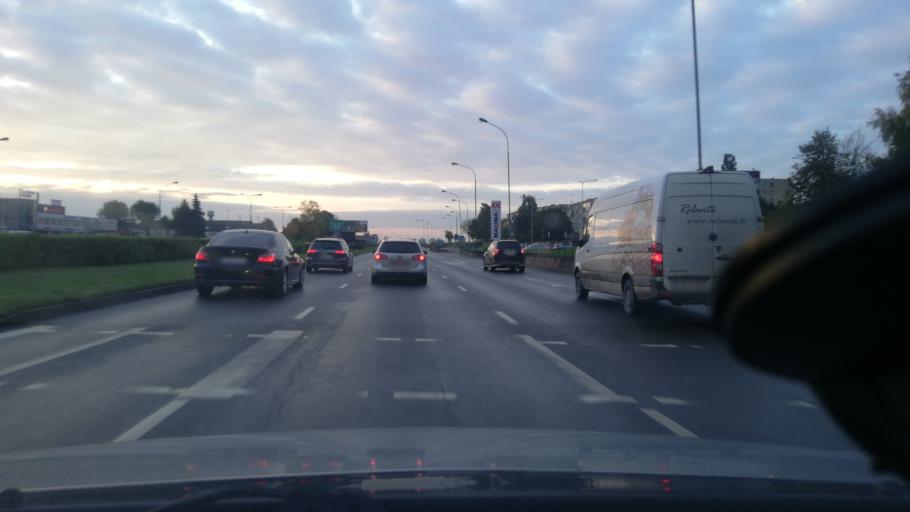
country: LT
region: Klaipedos apskritis
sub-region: Klaipeda
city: Klaipeda
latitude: 55.6900
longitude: 21.1801
